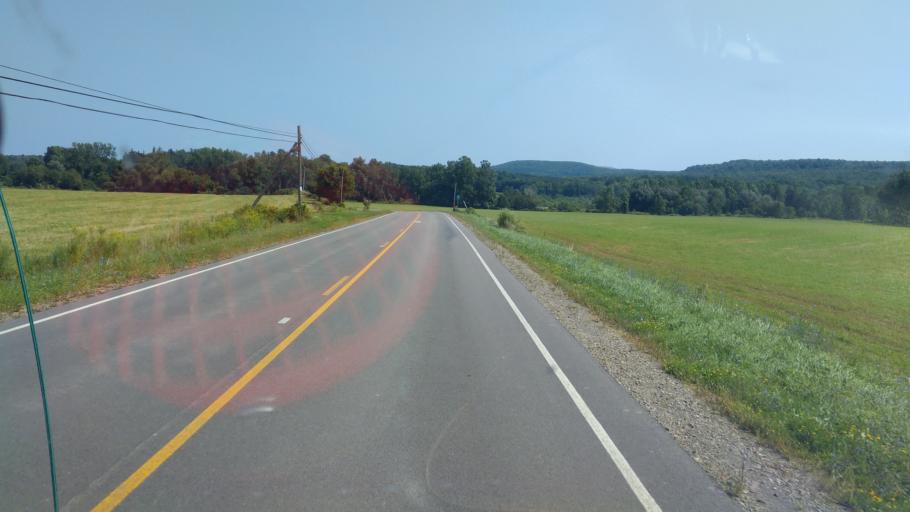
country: US
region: New York
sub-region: Allegany County
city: Belmont
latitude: 42.2593
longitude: -78.0542
